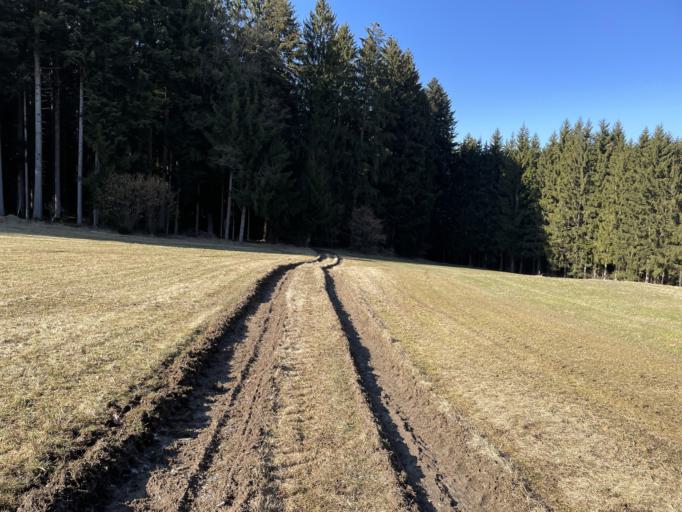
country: DE
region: Bavaria
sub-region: Lower Bavaria
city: Ruhmannsfelden
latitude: 48.9943
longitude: 13.0059
